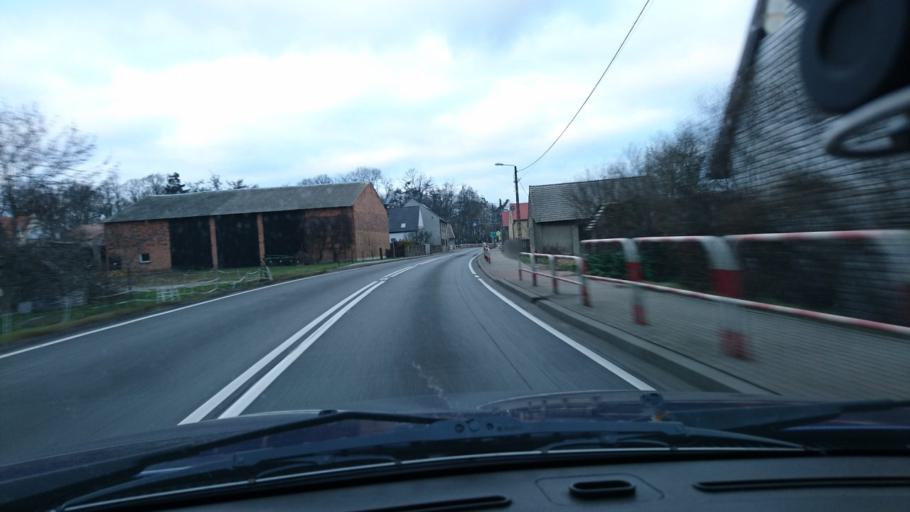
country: PL
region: Greater Poland Voivodeship
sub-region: Powiat kepinski
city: Opatow
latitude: 51.1783
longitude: 18.1432
